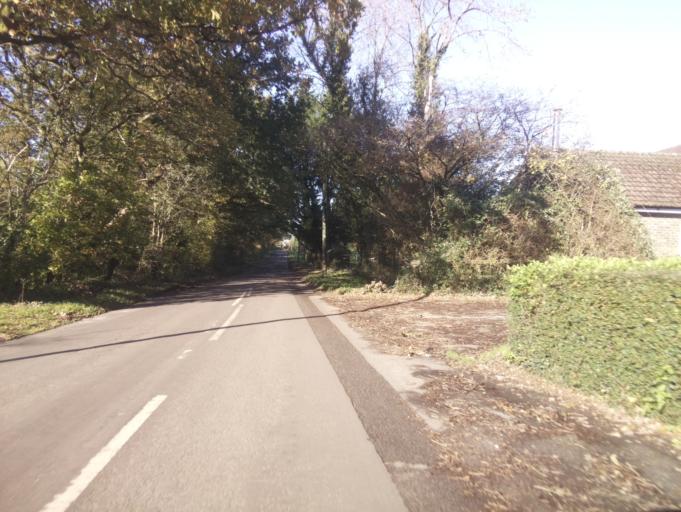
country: GB
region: England
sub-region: Dorset
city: Sherborne
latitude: 50.8653
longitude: -2.5184
